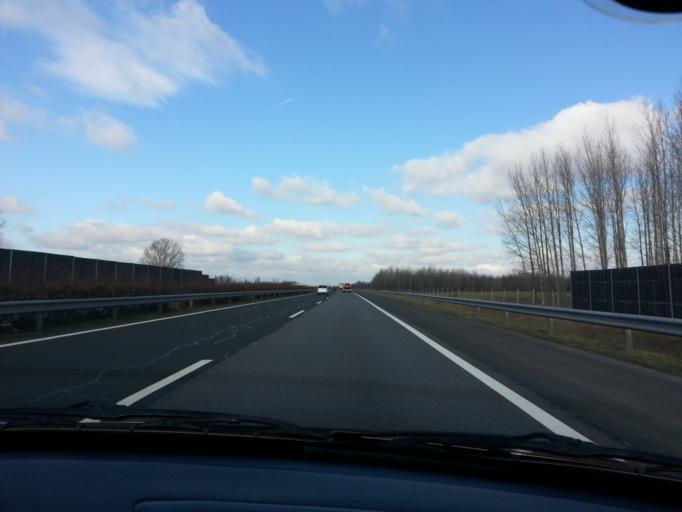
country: HU
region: Csongrad
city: Balastya
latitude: 46.3795
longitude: 19.9939
